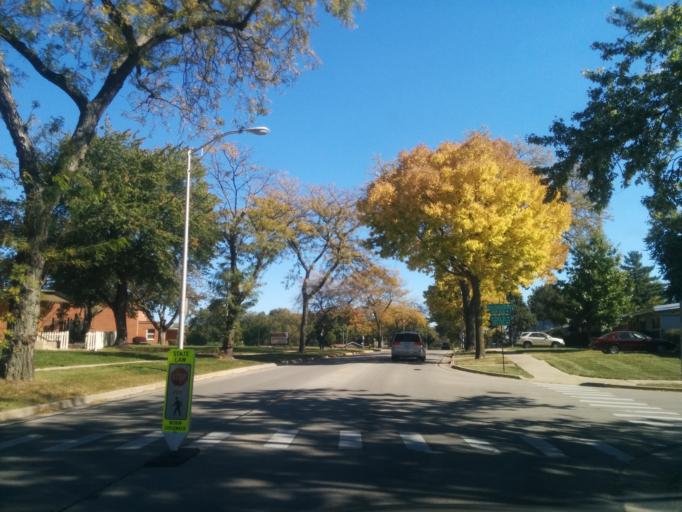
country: US
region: Illinois
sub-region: DuPage County
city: Lombard
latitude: 41.8748
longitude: -88.0226
